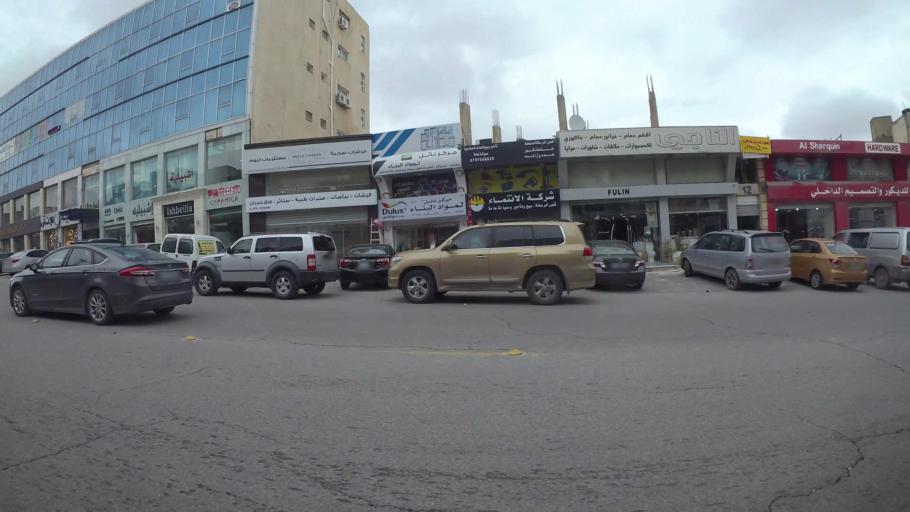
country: JO
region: Amman
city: Wadi as Sir
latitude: 31.9778
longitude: 35.8492
